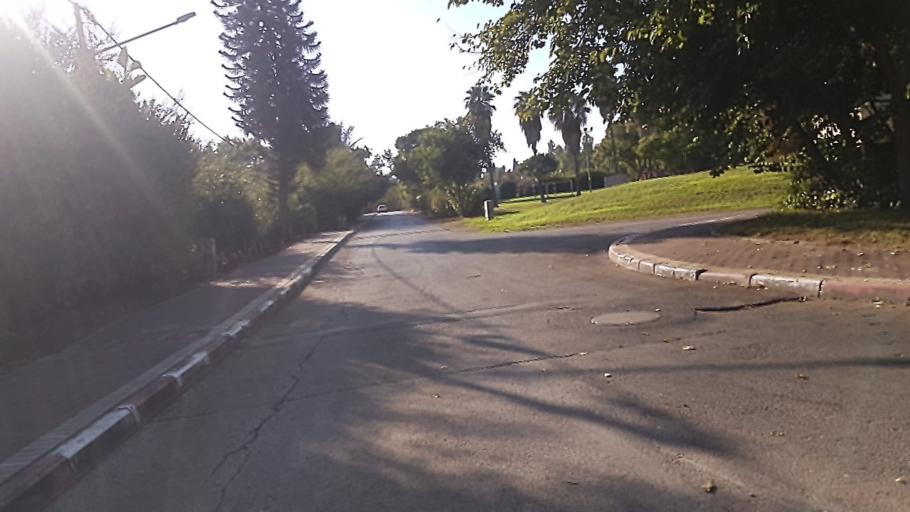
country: IL
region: Central District
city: Hod HaSharon
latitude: 32.1389
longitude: 34.9076
